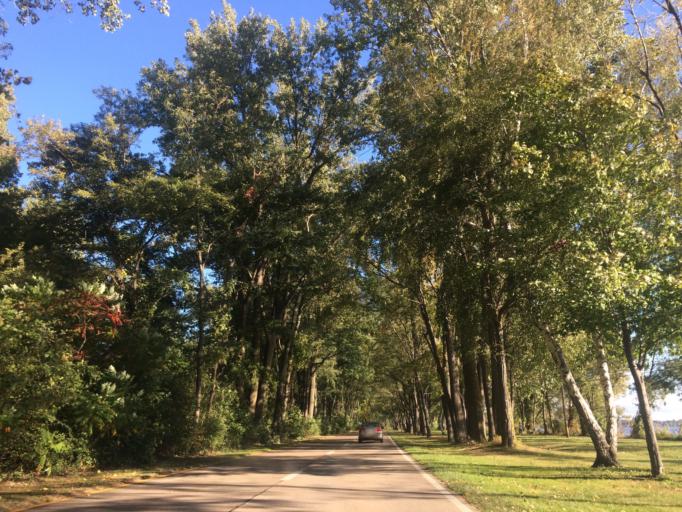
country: US
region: Pennsylvania
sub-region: Erie County
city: Erie
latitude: 42.1326
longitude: -80.1432
